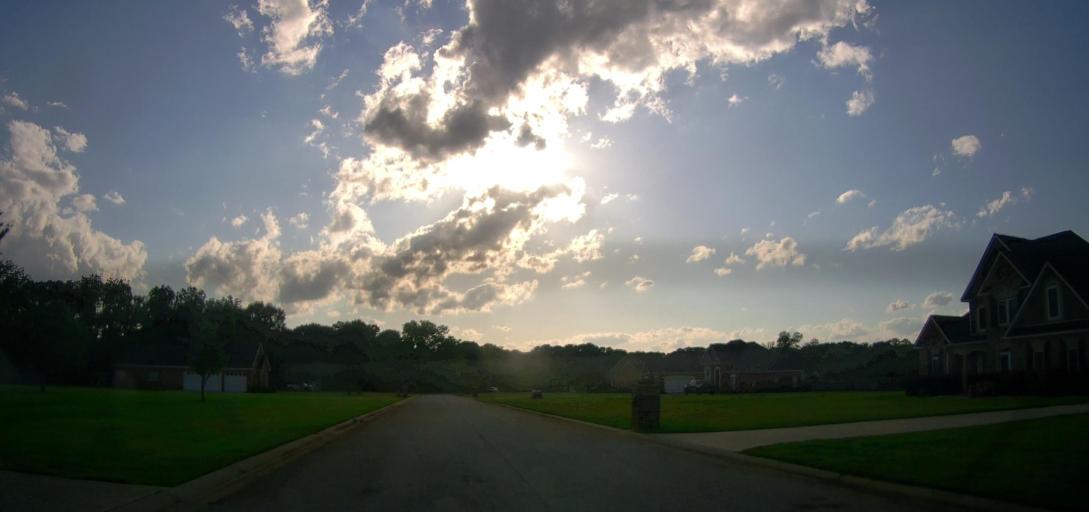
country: US
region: Georgia
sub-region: Peach County
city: Byron
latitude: 32.6486
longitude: -83.7925
